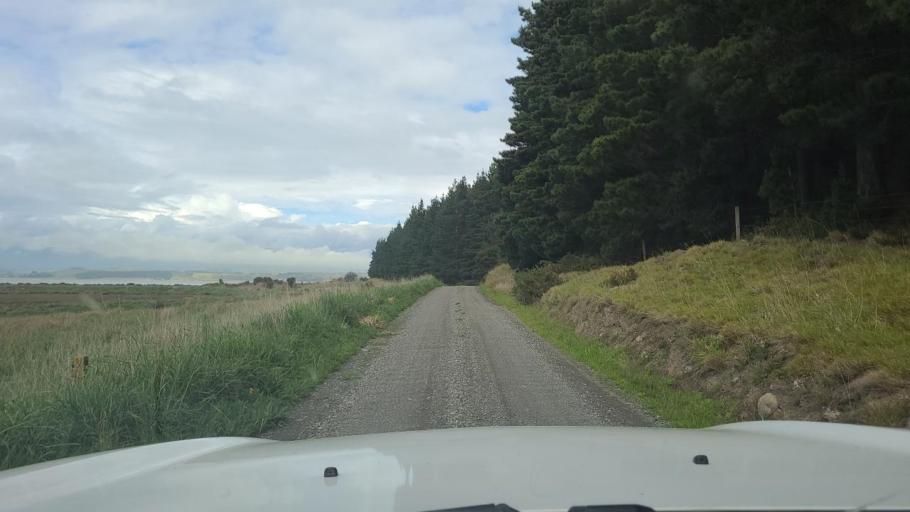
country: NZ
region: Wellington
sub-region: Upper Hutt City
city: Upper Hutt
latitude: -41.3753
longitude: 175.1049
